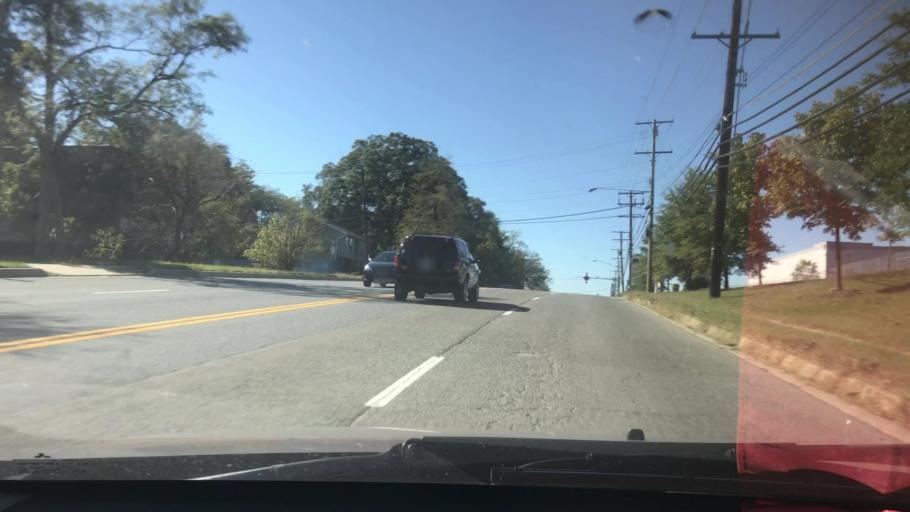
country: US
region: Maryland
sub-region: Prince George's County
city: Fairmount Heights
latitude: 38.9062
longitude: -76.9077
